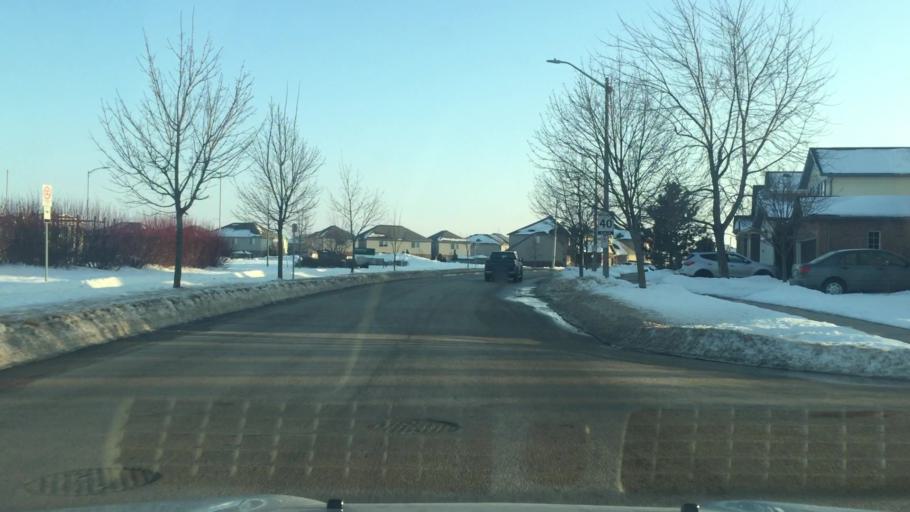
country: CA
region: Ontario
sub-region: Regional Municipality of Niagara
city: St. Catharines
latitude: 43.1765
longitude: -79.4704
